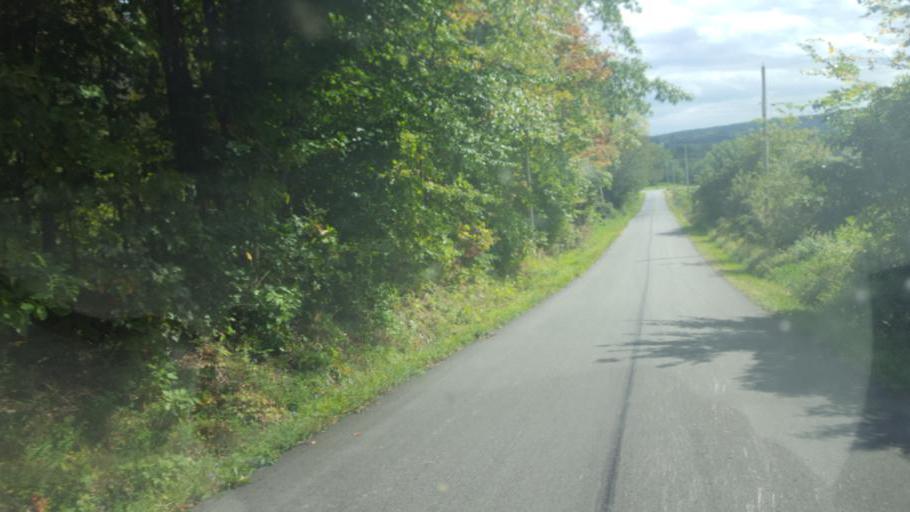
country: US
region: Pennsylvania
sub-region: Mercer County
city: Greenville
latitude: 41.5159
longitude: -80.3738
